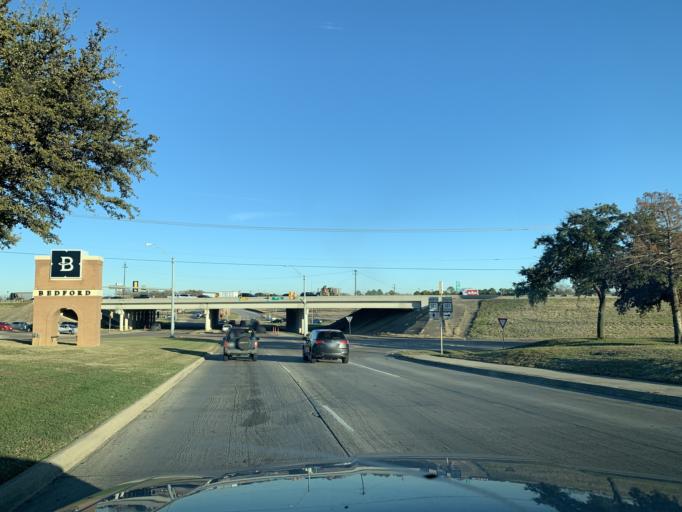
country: US
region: Texas
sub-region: Tarrant County
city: Bedford
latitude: 32.8518
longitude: -97.1123
